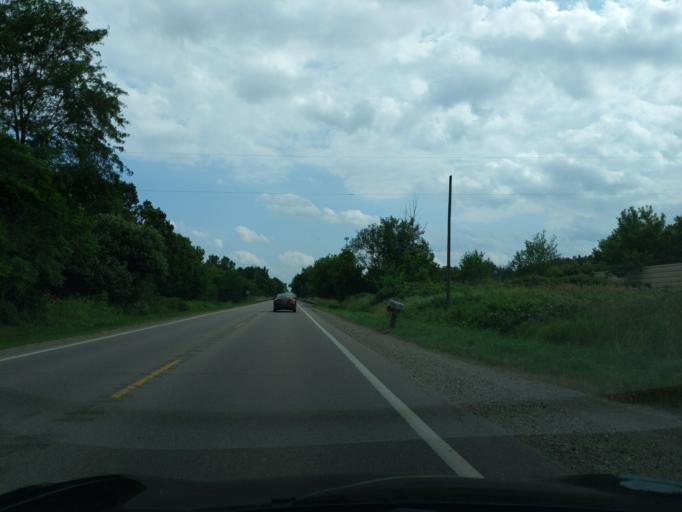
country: US
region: Michigan
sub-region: Eaton County
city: Eaton Rapids
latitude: 42.4457
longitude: -84.6497
